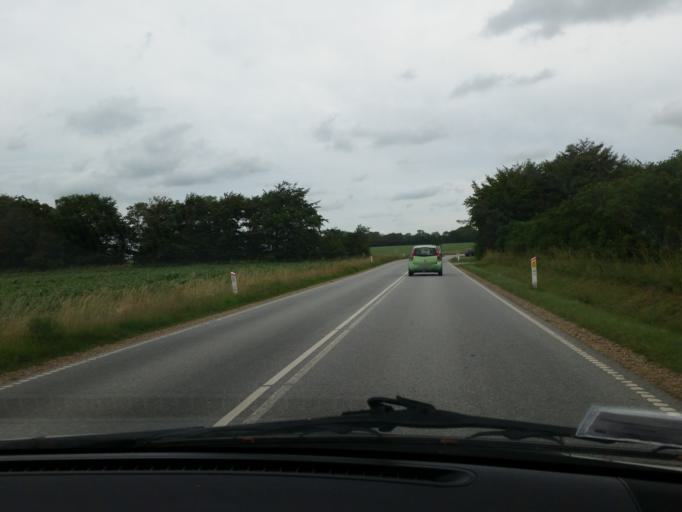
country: DK
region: South Denmark
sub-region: Esbjerg Kommune
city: Ribe
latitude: 55.3876
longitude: 8.8652
